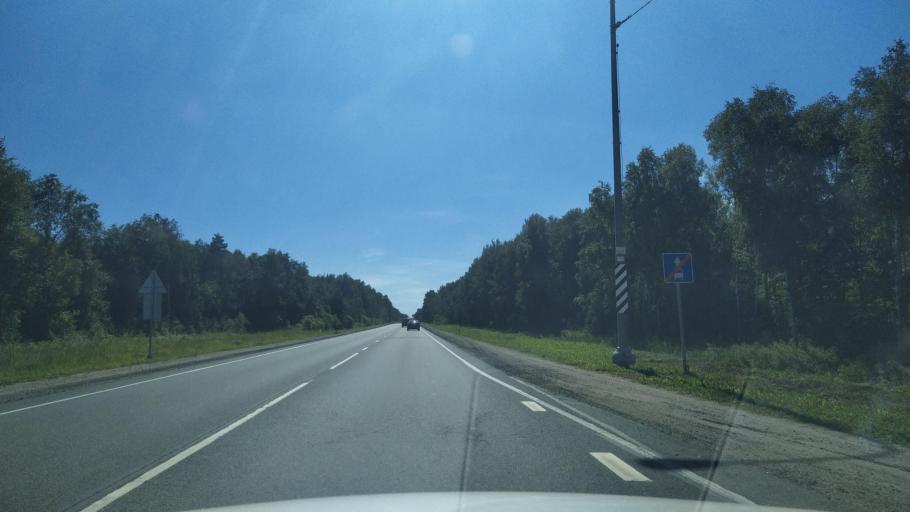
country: RU
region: Pskov
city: Pskov
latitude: 57.7779
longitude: 28.4014
